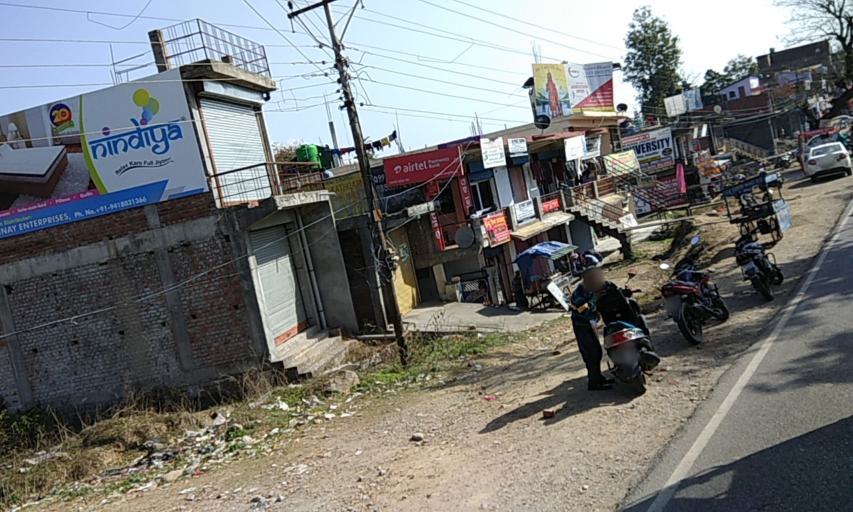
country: IN
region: Himachal Pradesh
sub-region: Kangra
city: Yol
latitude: 32.2153
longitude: 76.1807
